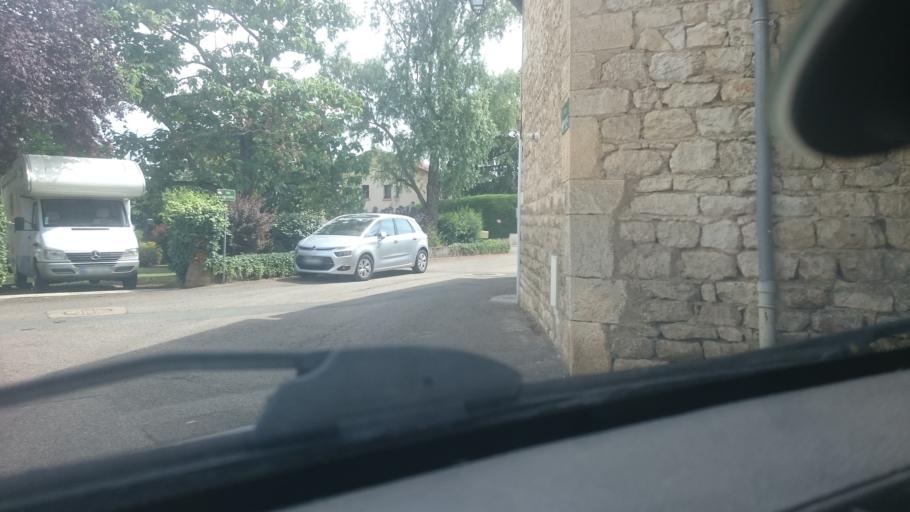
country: FR
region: Rhone-Alpes
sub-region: Departement du Rhone
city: Lucenay
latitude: 45.9095
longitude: 4.7041
